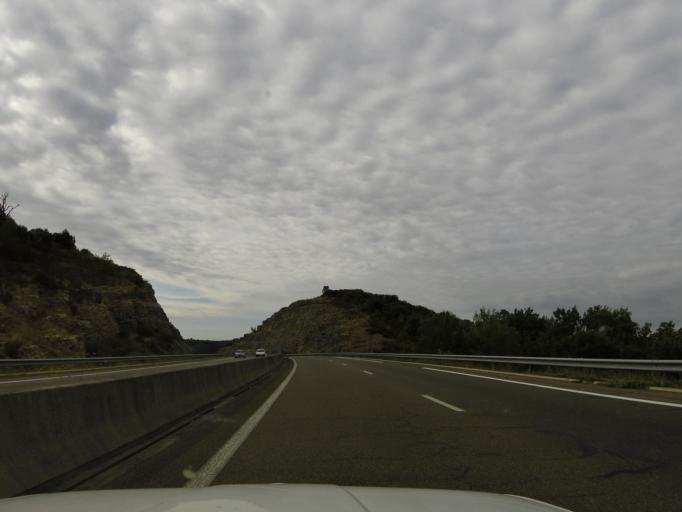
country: FR
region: Languedoc-Roussillon
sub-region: Departement du Gard
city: Vezenobres
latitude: 44.0251
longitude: 4.1469
